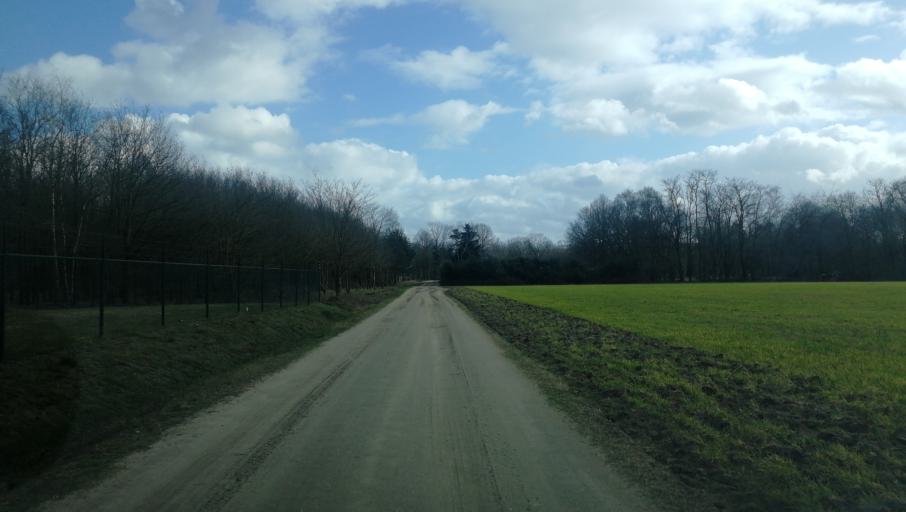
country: NL
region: Limburg
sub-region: Gemeente Venlo
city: Venlo
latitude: 51.3995
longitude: 6.1191
